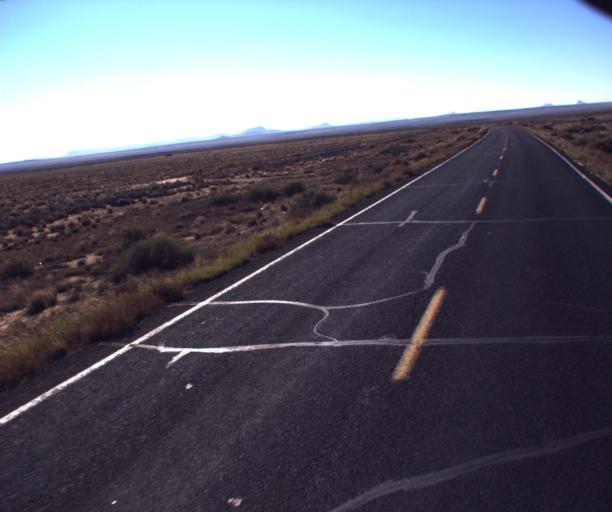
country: US
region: Arizona
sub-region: Navajo County
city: First Mesa
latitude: 35.7330
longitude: -110.5188
